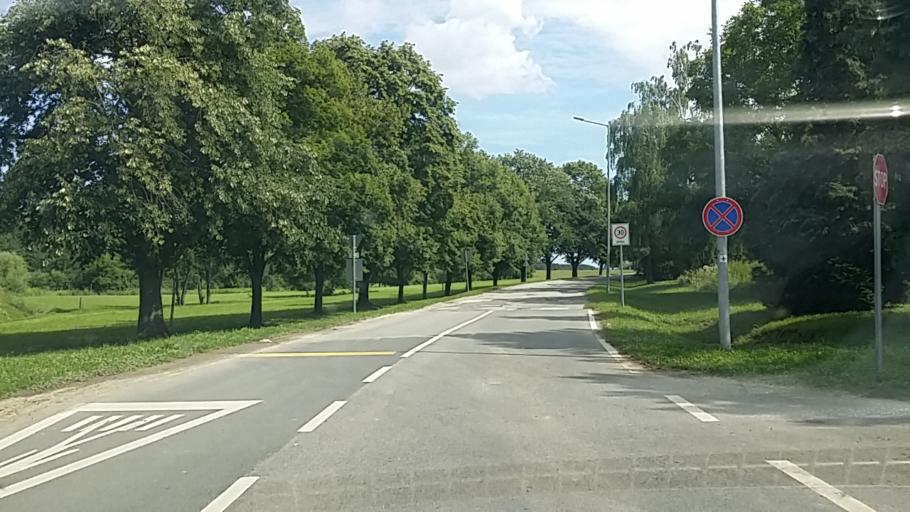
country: HU
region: Zala
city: Nagykanizsa
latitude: 46.4429
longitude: 17.0337
